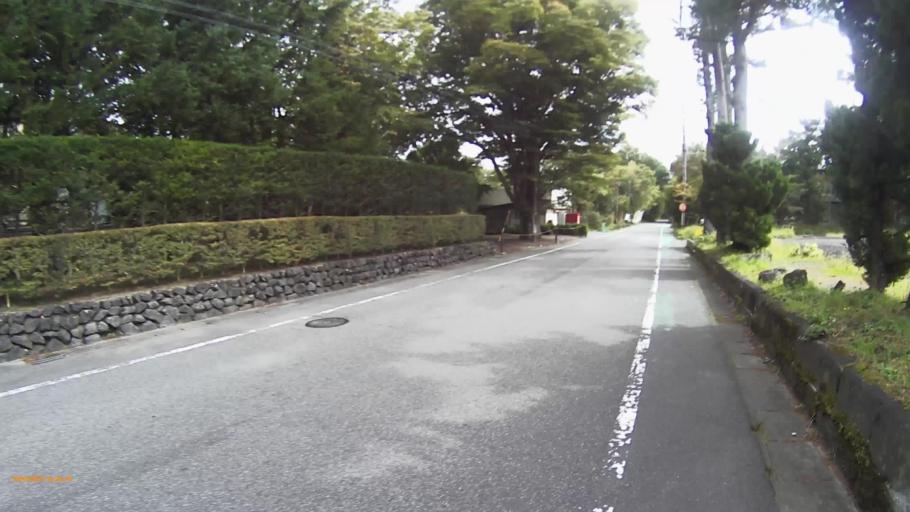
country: JP
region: Shizuoka
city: Gotemba
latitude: 35.4156
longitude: 138.8561
